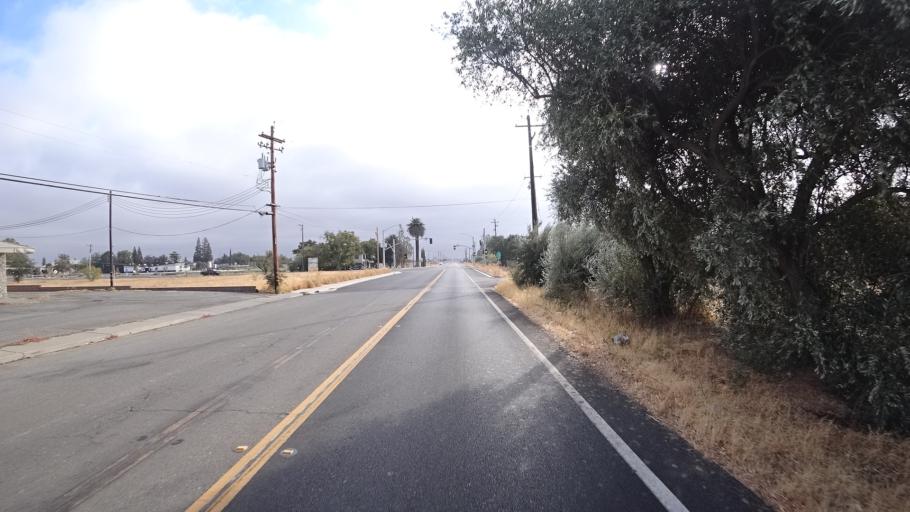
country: US
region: California
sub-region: Yolo County
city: Esparto
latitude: 38.6892
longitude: -122.0187
